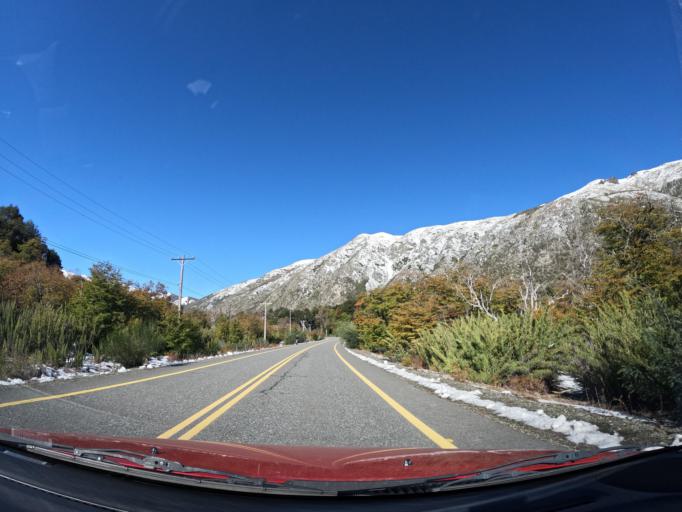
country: CL
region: Biobio
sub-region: Provincia de Nuble
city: Coihueco
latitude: -36.9124
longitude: -71.4738
